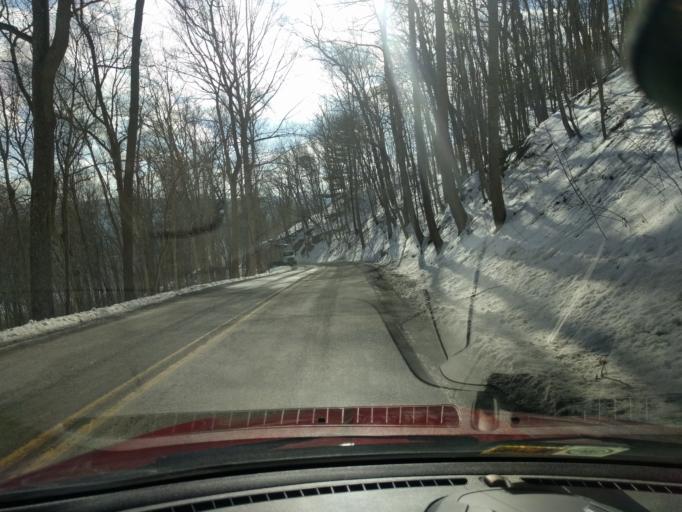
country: US
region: Virginia
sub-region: Bath County
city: Warm Springs
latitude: 38.0935
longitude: -79.8404
